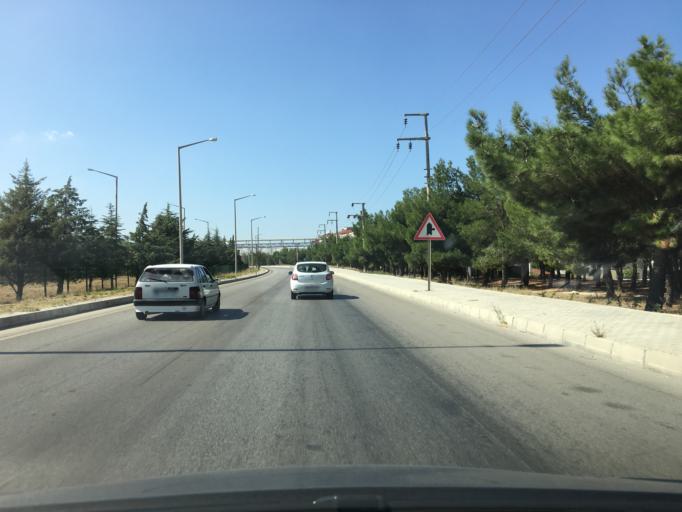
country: TR
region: Burdur
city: Burdur
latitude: 37.7289
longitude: 30.3037
